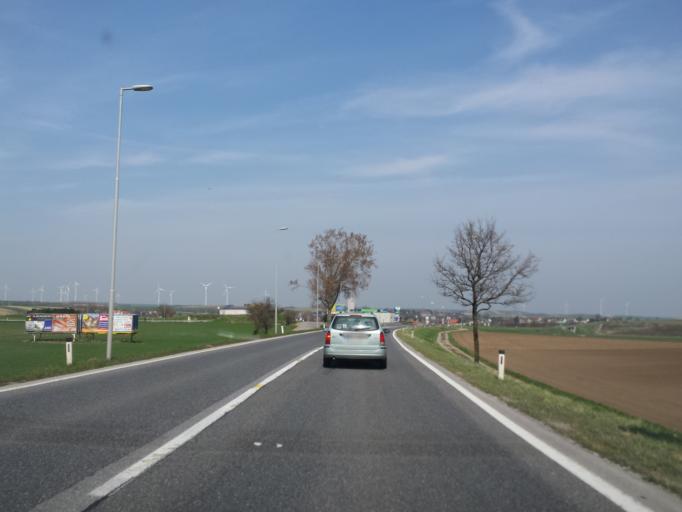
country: AT
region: Lower Austria
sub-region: Politischer Bezirk Mistelbach
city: Wilfersdorf
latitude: 48.5703
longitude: 16.6386
